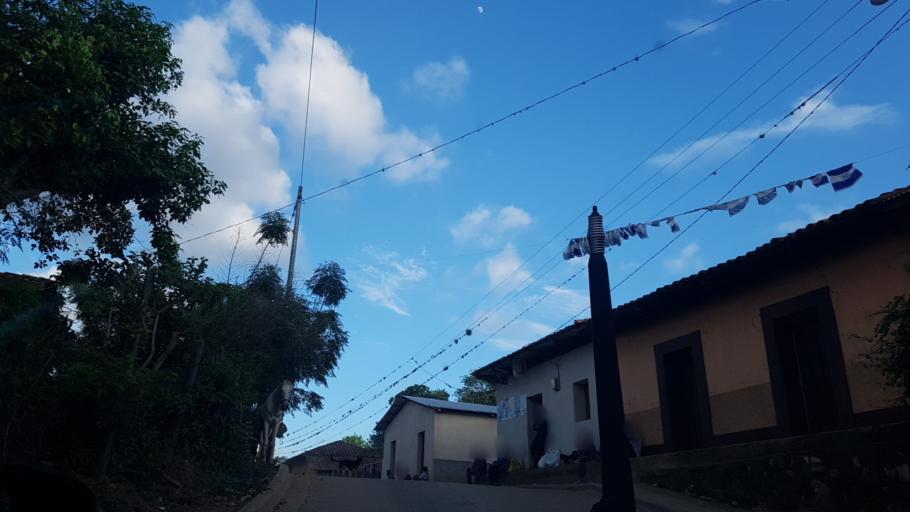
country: NI
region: Nueva Segovia
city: Ocotal
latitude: 13.6526
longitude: -86.6136
